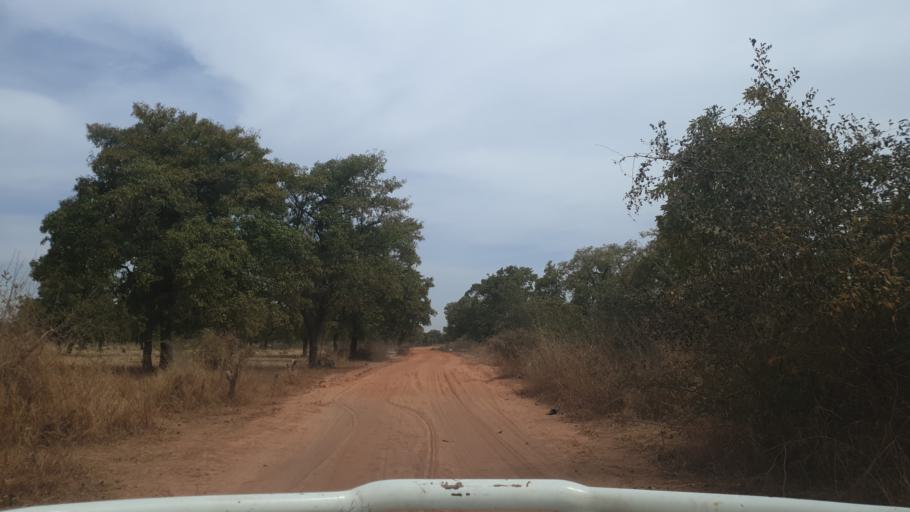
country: ML
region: Sikasso
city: Yorosso
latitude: 12.2279
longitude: -4.7501
